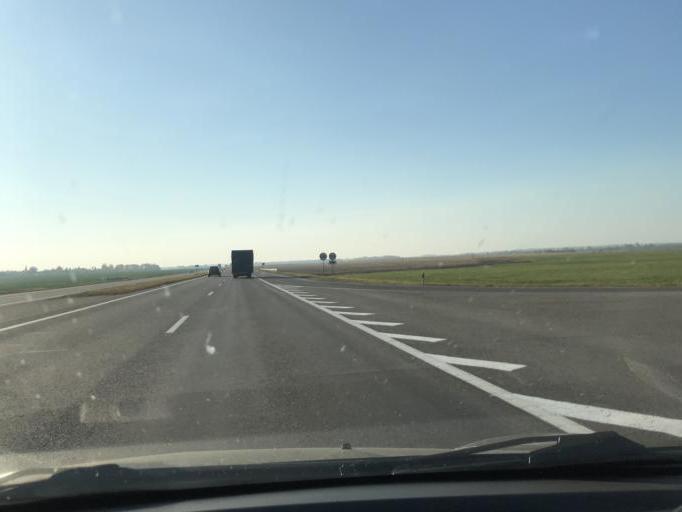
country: BY
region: Minsk
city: Machulishchy
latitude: 53.7396
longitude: 27.6076
